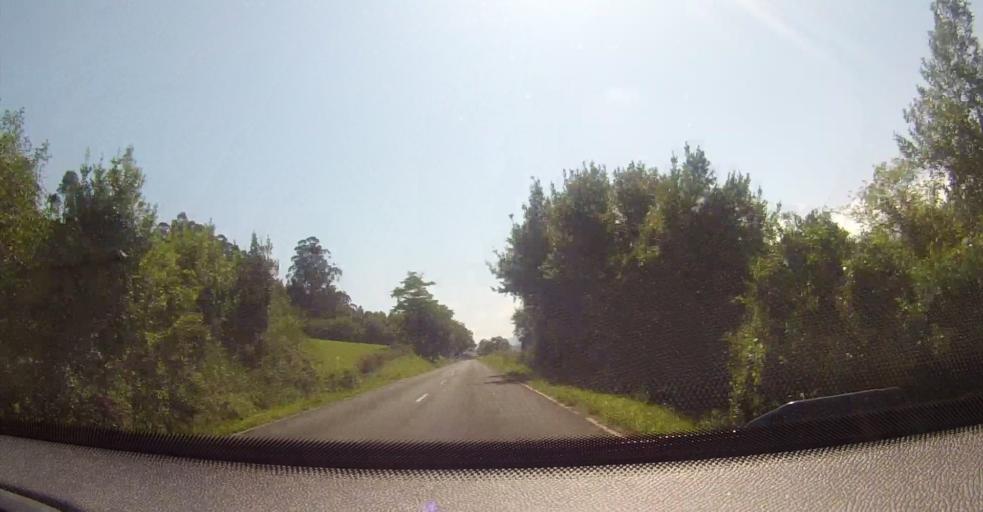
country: ES
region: Asturias
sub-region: Province of Asturias
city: Colunga
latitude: 43.4882
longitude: -5.2999
